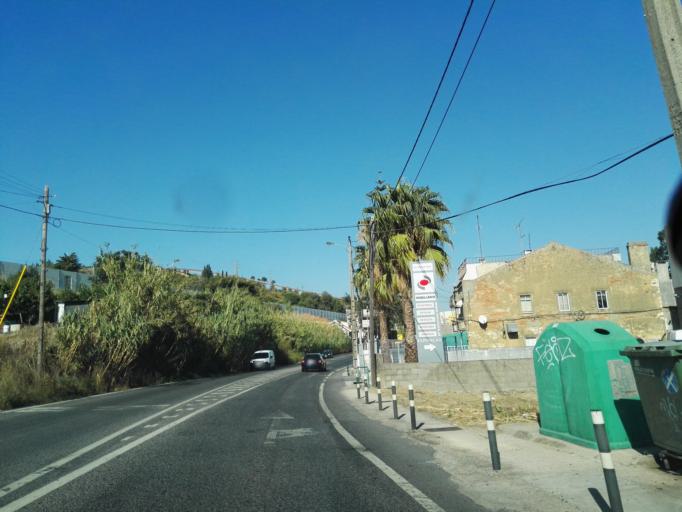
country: PT
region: Lisbon
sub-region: Vila Franca de Xira
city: Sobralinho
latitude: 38.9165
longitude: -9.0208
